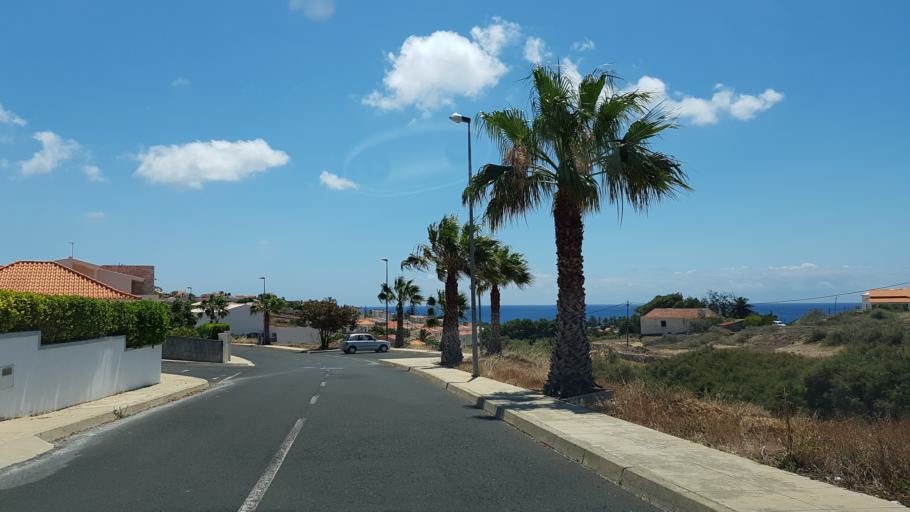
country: PT
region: Madeira
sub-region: Porto Santo
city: Vila de Porto Santo
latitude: 33.0553
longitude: -16.3538
